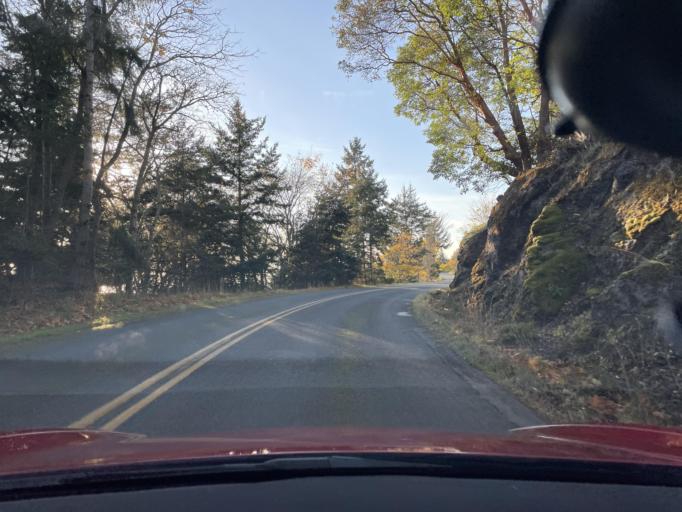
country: US
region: Washington
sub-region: San Juan County
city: Friday Harbor
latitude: 48.5138
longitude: -123.1455
